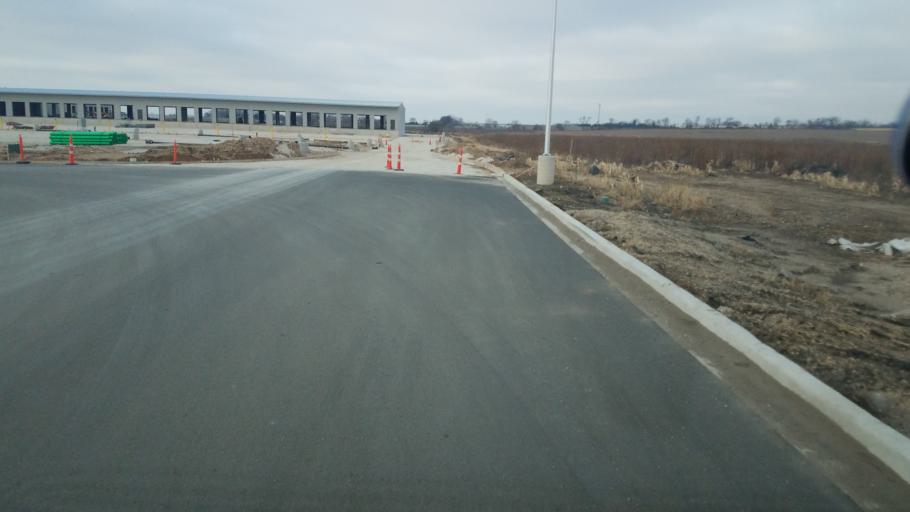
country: US
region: Illinois
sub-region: Kane County
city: Hampshire
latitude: 42.1500
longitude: -88.5194
